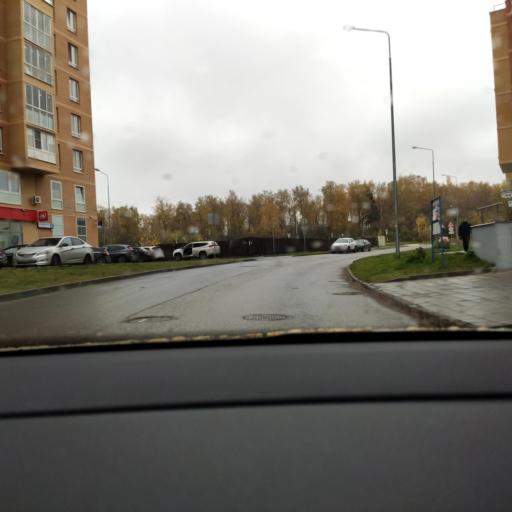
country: RU
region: Moskovskaya
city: Shcherbinka
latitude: 55.5007
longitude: 37.5414
